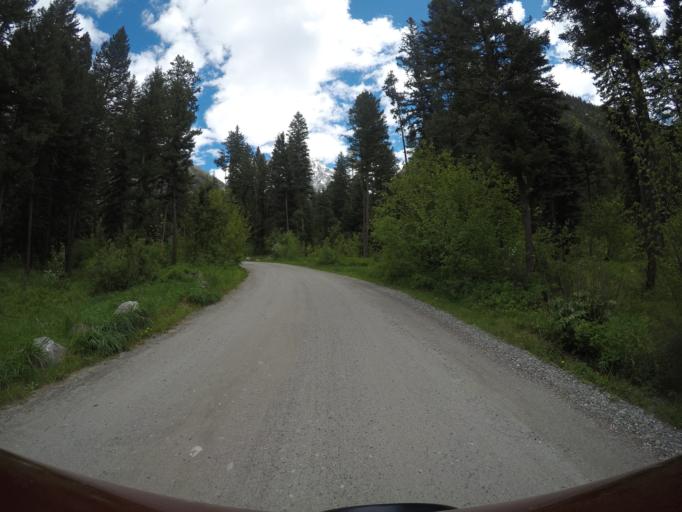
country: US
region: Montana
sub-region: Park County
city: Livingston
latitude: 45.4974
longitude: -110.5213
